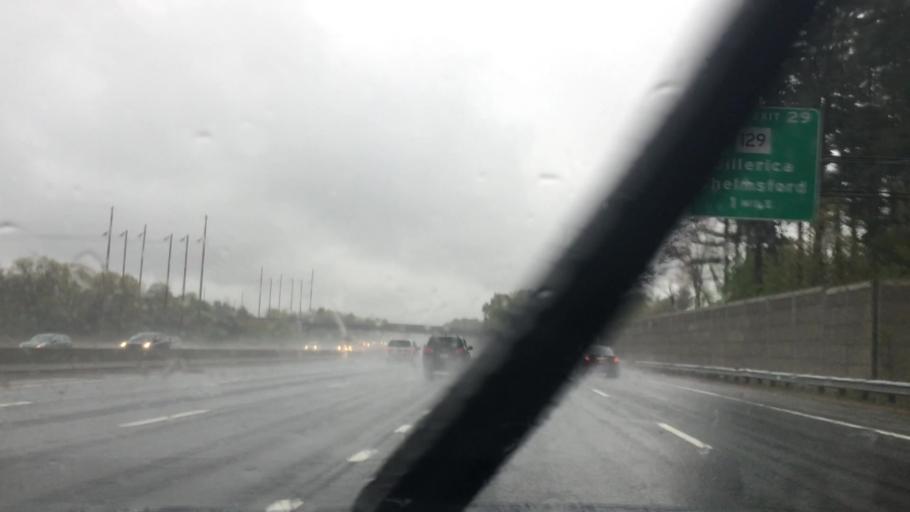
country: US
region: Massachusetts
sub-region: Middlesex County
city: Lowell
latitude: 42.6022
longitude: -71.3235
